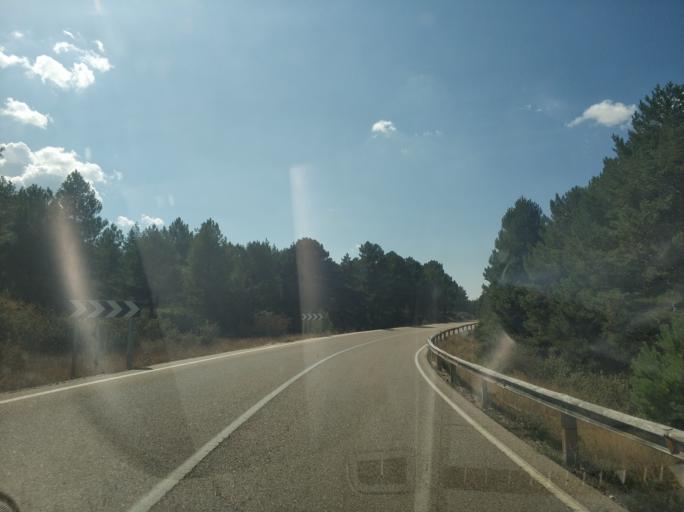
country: ES
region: Castille and Leon
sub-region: Provincia de Soria
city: Herrera de Soria
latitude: 41.7662
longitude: -3.0313
